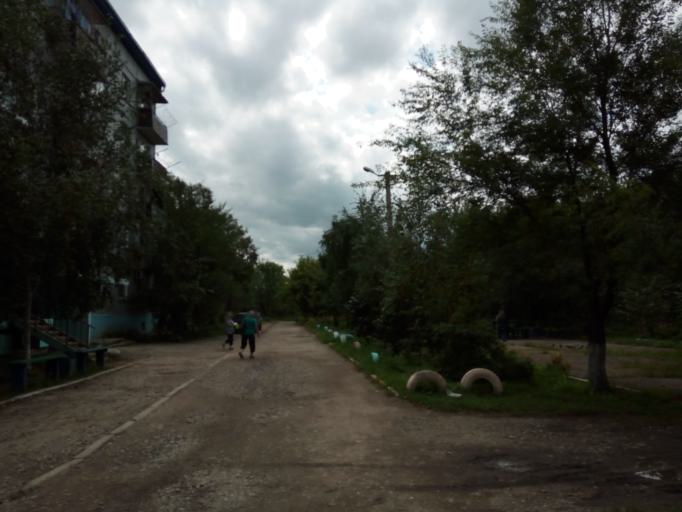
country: RU
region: Primorskiy
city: Dal'nerechensk
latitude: 45.9417
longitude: 133.8145
